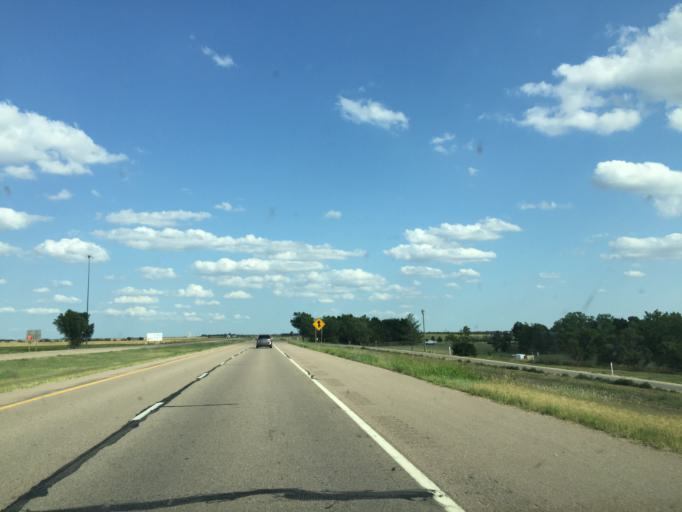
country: US
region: Kansas
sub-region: Gove County
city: Gove
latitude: 39.0575
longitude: -100.2410
